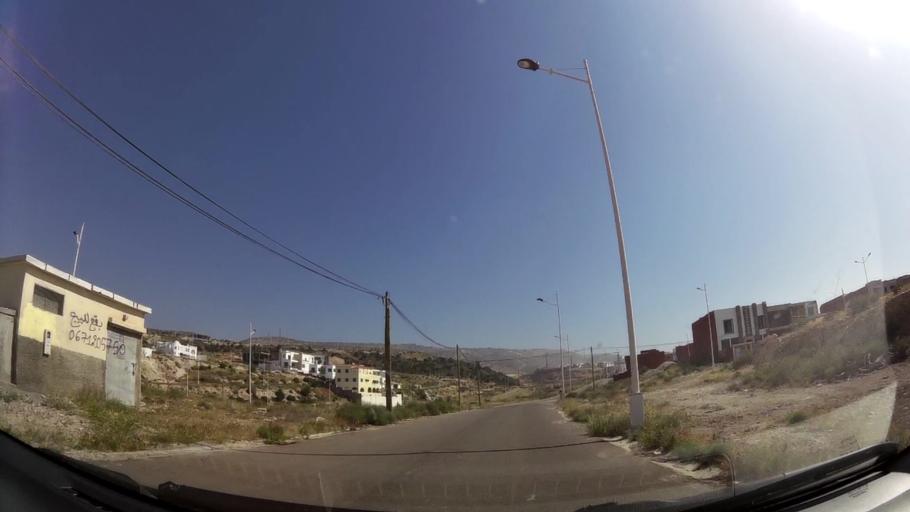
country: MA
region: Souss-Massa-Draa
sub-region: Agadir-Ida-ou-Tnan
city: Agadir
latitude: 30.4409
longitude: -9.5764
